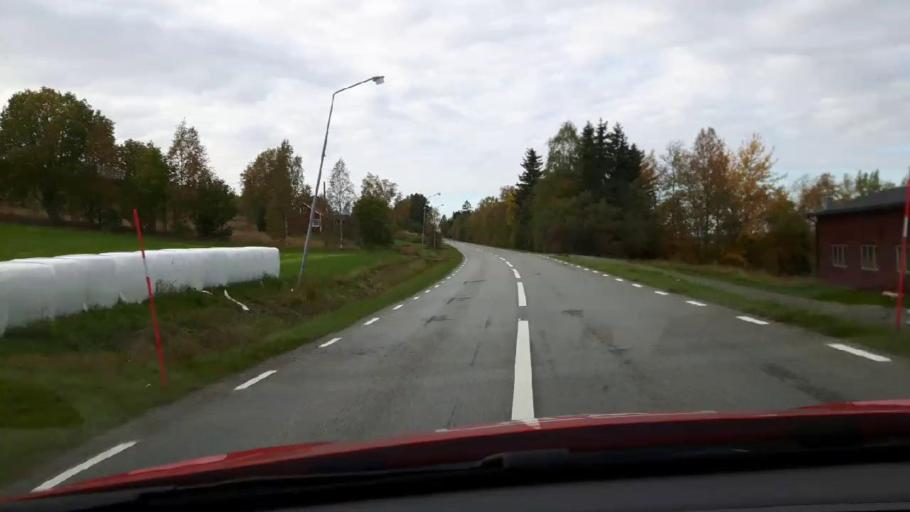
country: SE
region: Jaemtland
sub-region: Krokoms Kommun
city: Krokom
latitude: 63.1812
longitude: 14.0845
